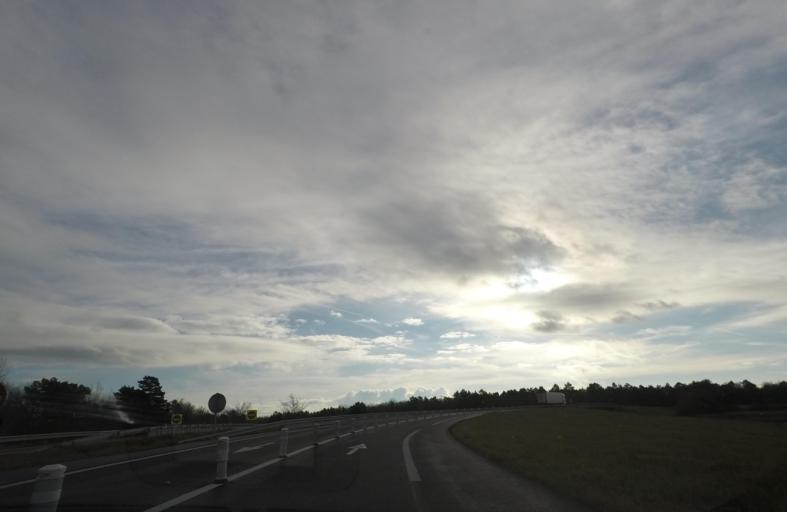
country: FR
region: Centre
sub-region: Departement du Loir-et-Cher
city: Villefranche-sur-Cher
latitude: 47.3226
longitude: 1.7683
